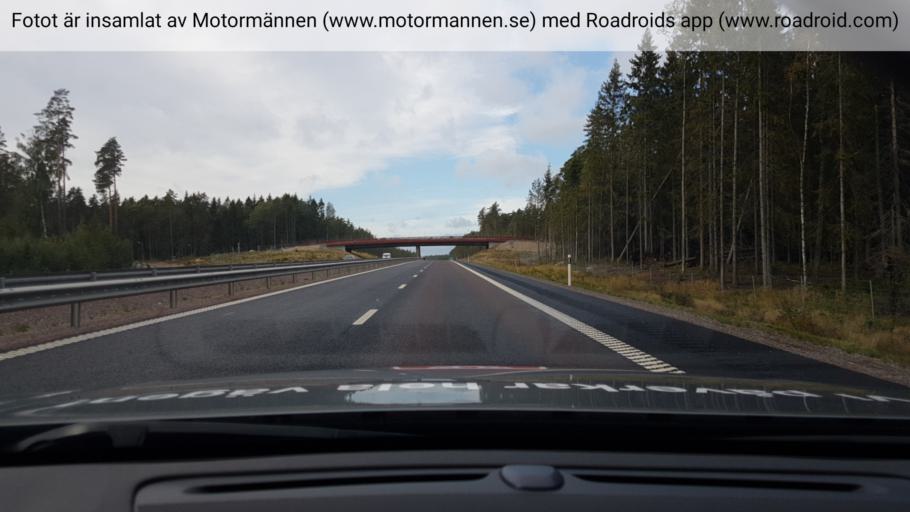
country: SE
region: Vaermland
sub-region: Hammaro Kommun
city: Skoghall
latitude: 59.3821
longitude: 13.3754
